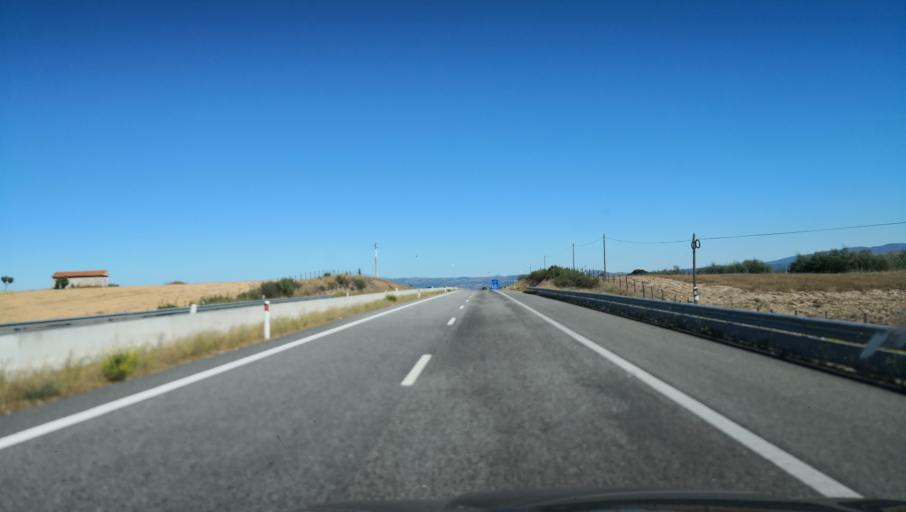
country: PT
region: Braganca
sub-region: Mirandela
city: Mirandela
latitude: 41.4695
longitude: -7.2363
